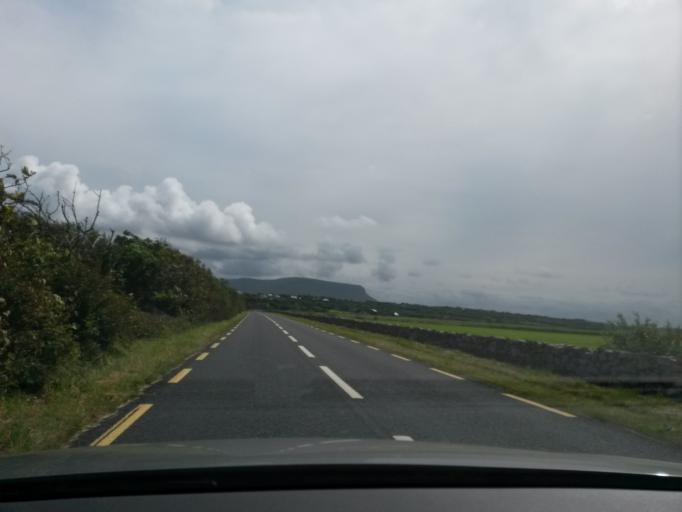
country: IE
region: Connaught
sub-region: Sligo
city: Sligo
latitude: 54.4408
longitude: -8.4551
